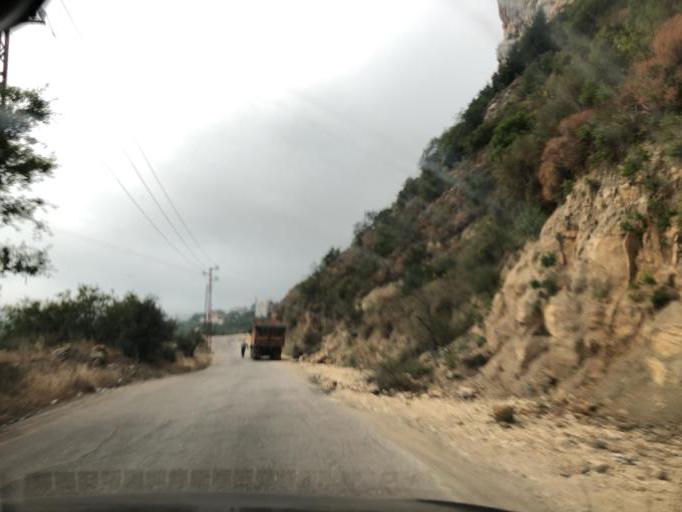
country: LB
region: Liban-Nord
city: Bcharre
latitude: 34.1134
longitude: 35.9074
